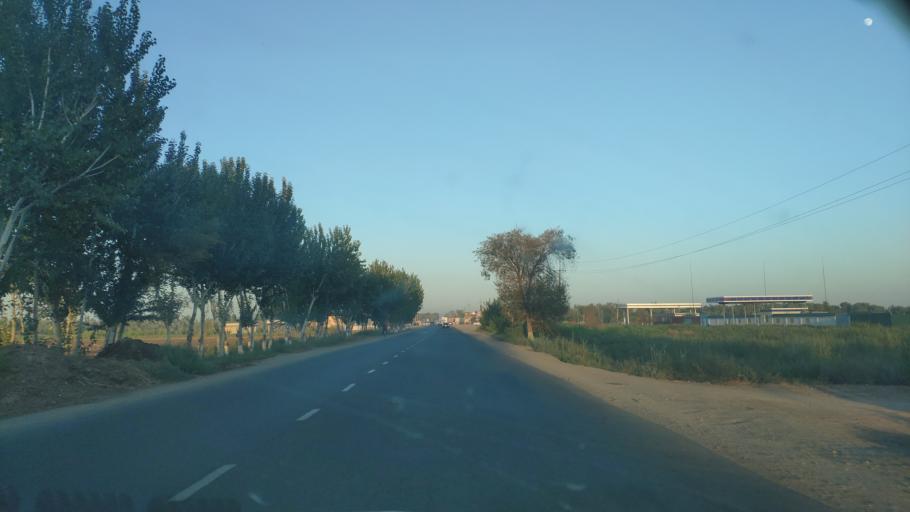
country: UZ
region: Karakalpakstan
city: To'rtko'l Shahri
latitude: 41.5696
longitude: 60.9462
